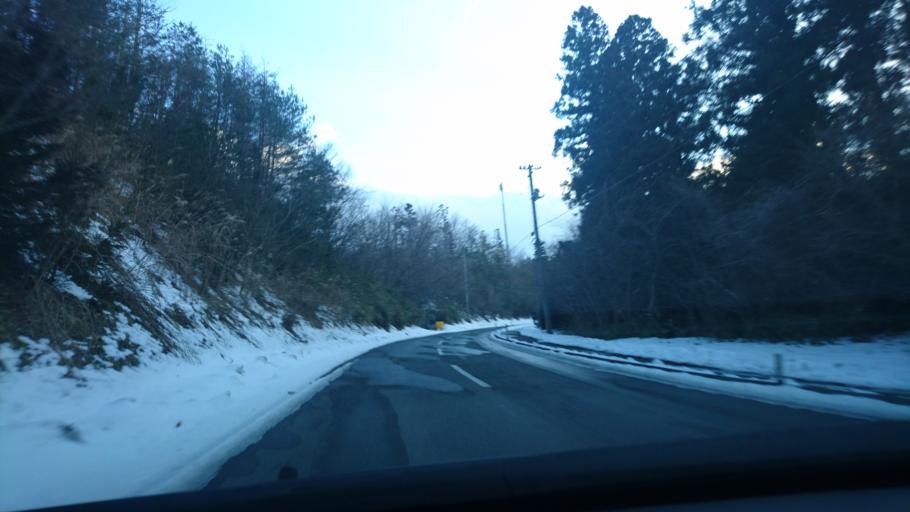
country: JP
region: Iwate
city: Ichinoseki
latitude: 39.0130
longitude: 141.3388
